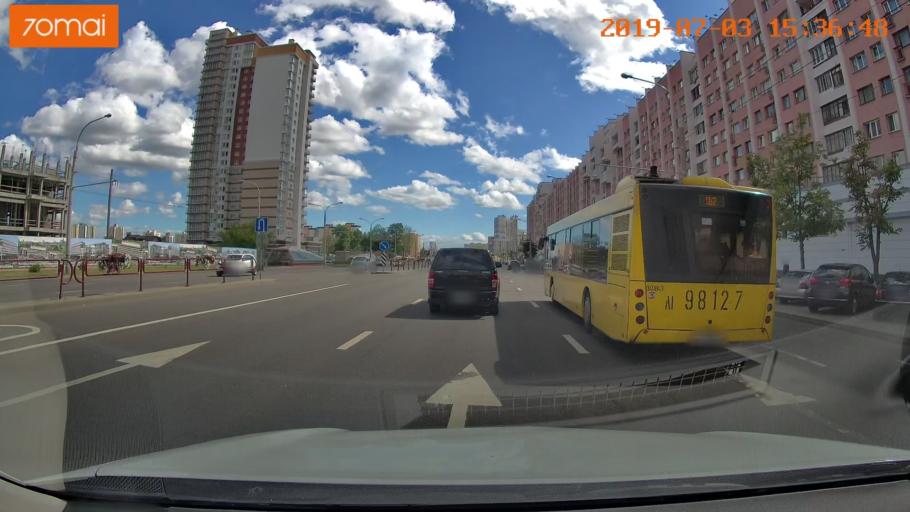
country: BY
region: Minsk
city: Minsk
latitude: 53.8803
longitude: 27.5681
